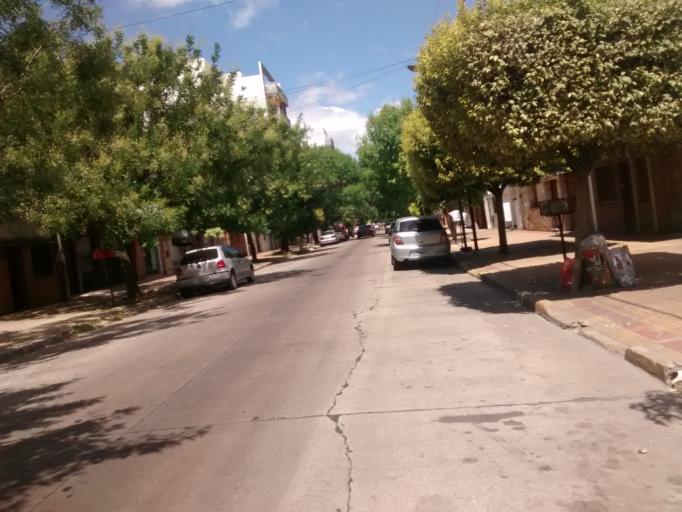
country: AR
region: Buenos Aires
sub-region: Partido de La Plata
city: La Plata
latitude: -34.9090
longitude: -57.9737
